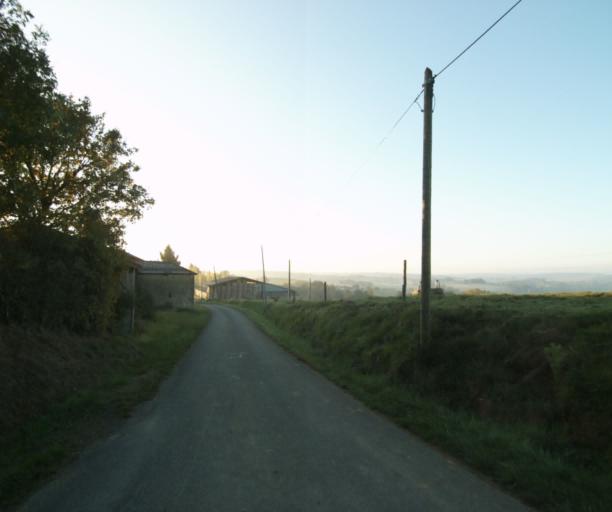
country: FR
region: Midi-Pyrenees
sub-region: Departement du Gers
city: Eauze
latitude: 43.7823
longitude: 0.1728
